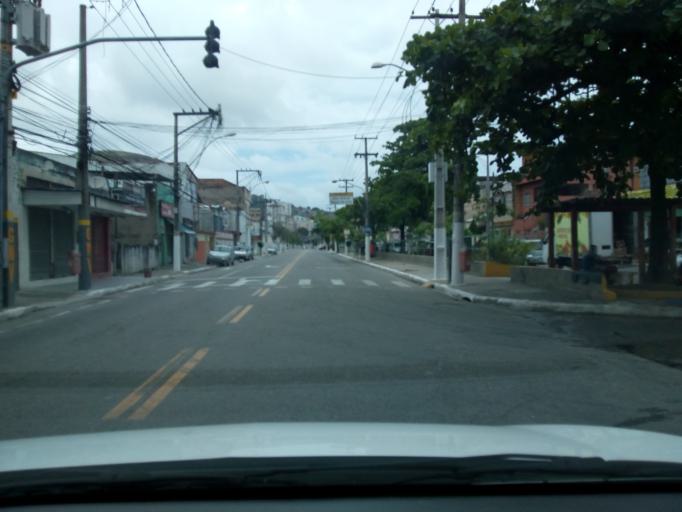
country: BR
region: Rio de Janeiro
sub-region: Niteroi
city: Niteroi
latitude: -22.8661
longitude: -43.1037
